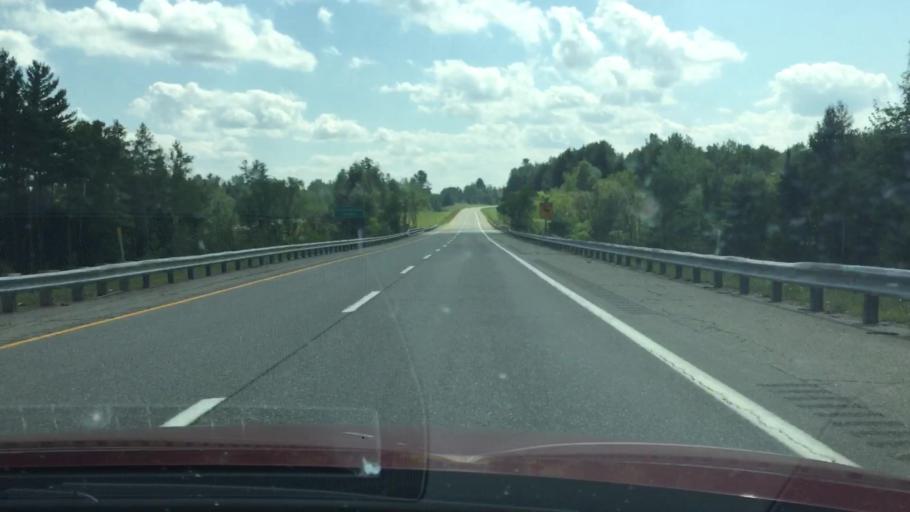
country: US
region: Maine
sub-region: Penobscot County
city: Lincoln
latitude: 45.3644
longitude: -68.6060
